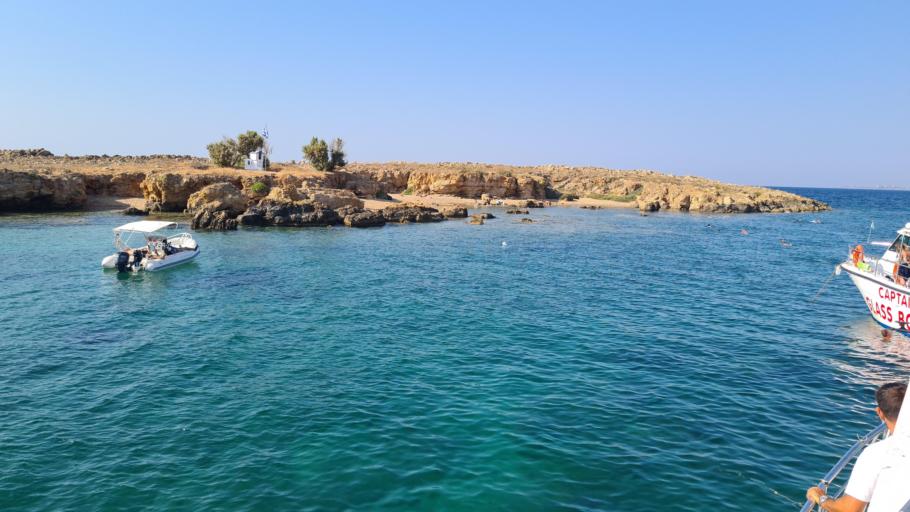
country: GR
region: Crete
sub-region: Nomos Chanias
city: Chania
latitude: 35.5183
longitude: 23.9997
